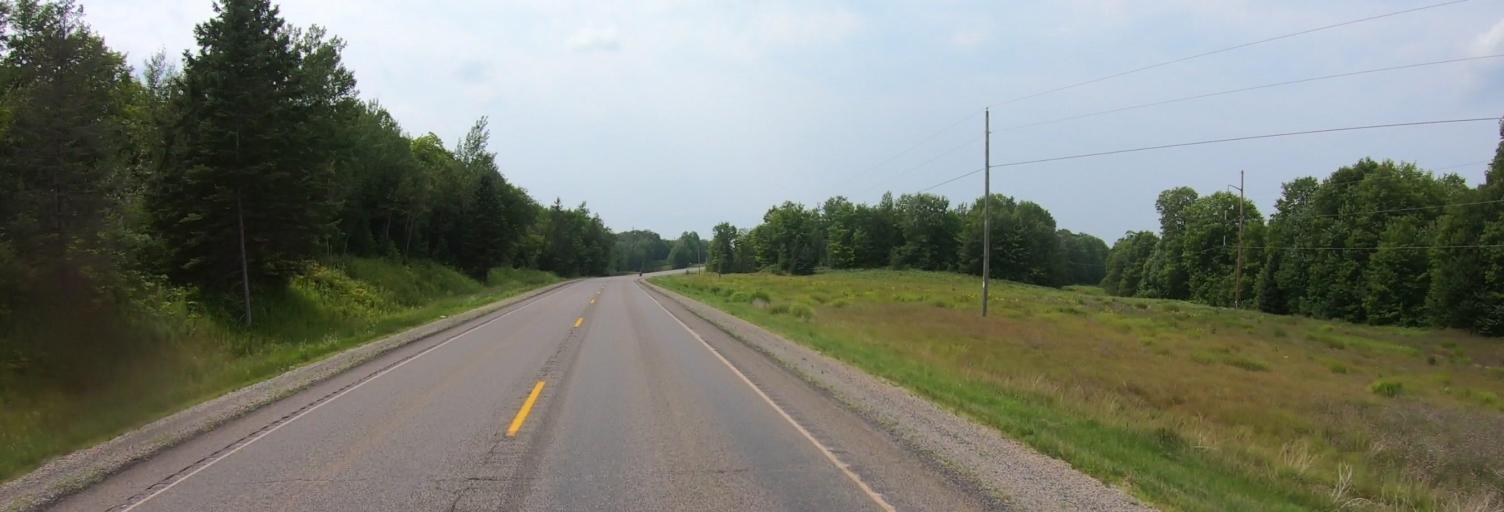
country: US
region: Michigan
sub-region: Alger County
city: Munising
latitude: 46.3320
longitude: -86.8612
